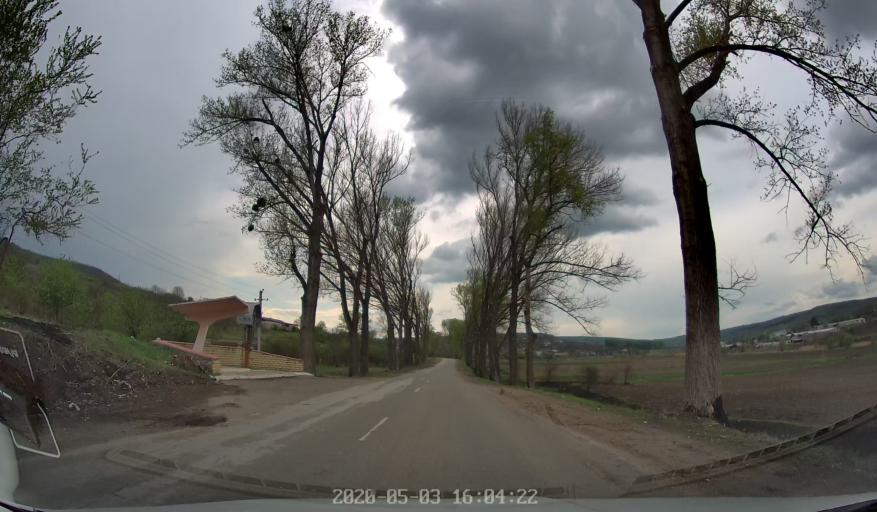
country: MD
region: Stinga Nistrului
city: Bucovat
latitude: 47.1861
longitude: 28.3686
